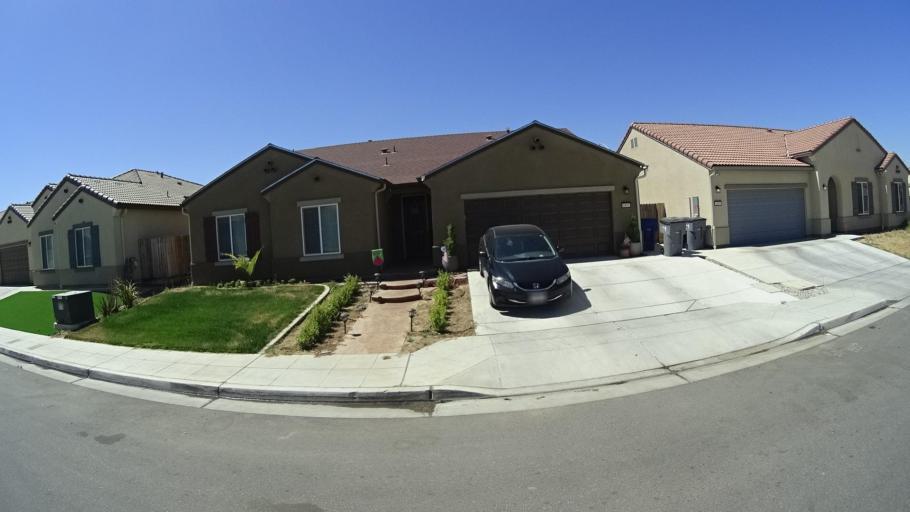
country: US
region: California
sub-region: Fresno County
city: Sunnyside
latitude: 36.7212
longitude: -119.6663
